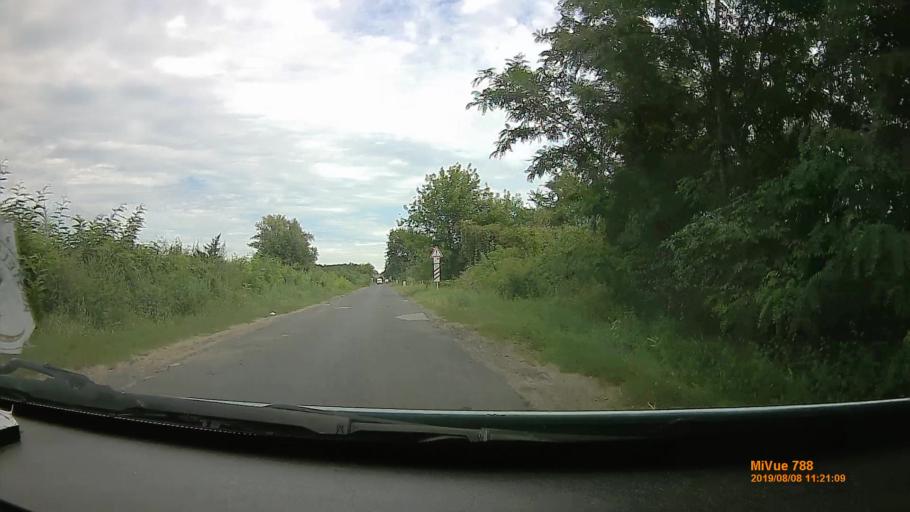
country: HU
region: Szabolcs-Szatmar-Bereg
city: Balkany
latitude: 47.7557
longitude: 21.8462
